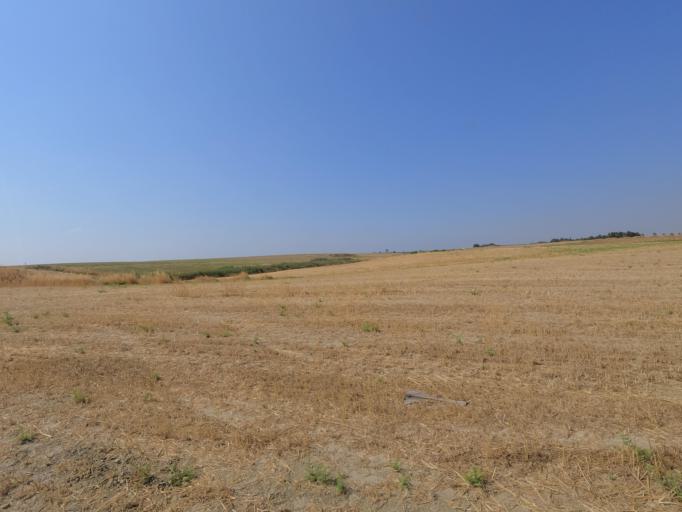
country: CY
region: Larnaka
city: Dhromolaxia
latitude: 34.9020
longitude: 33.5875
